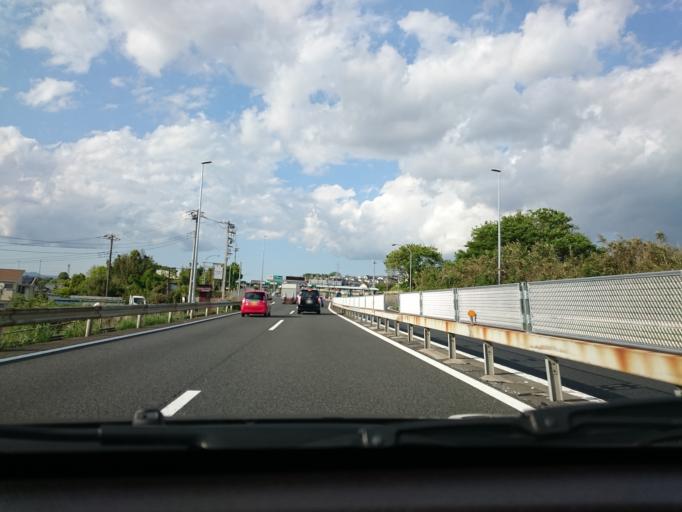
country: JP
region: Kanagawa
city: Oiso
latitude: 35.3351
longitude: 139.2944
